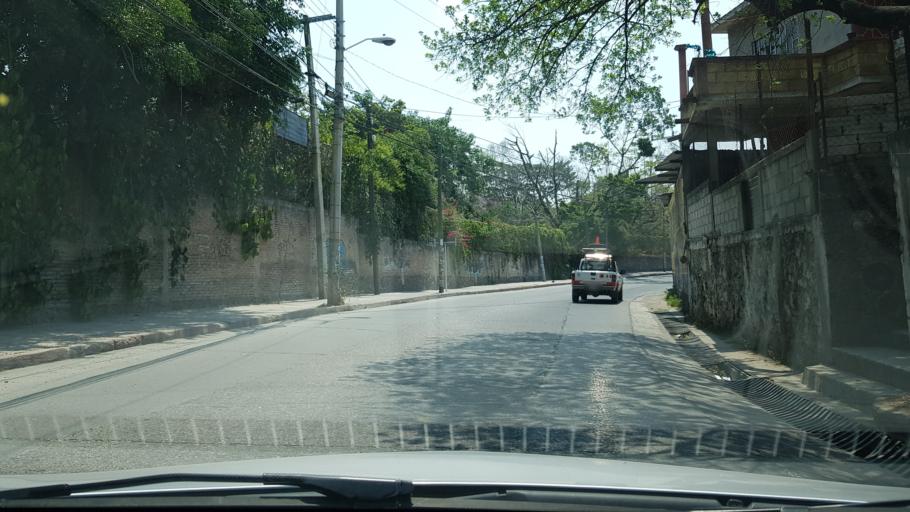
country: MX
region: Morelos
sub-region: Jiutepec
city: Jiutepec
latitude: 18.8773
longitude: -99.1734
